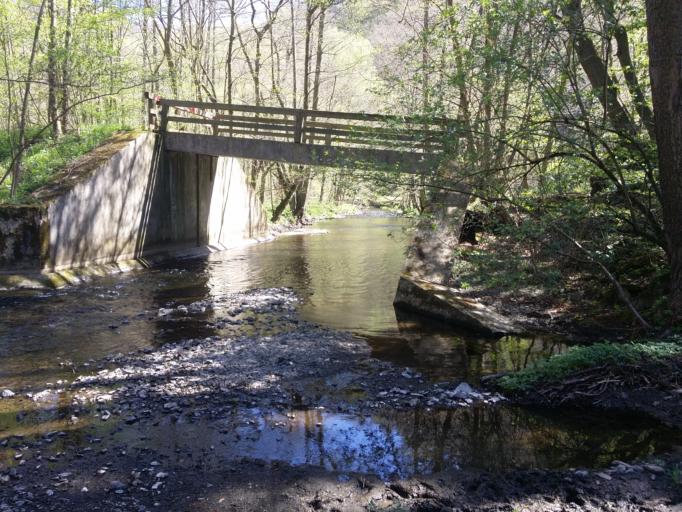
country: DE
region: Saxony-Anhalt
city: Ballenstedt
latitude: 51.6787
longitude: 11.2331
